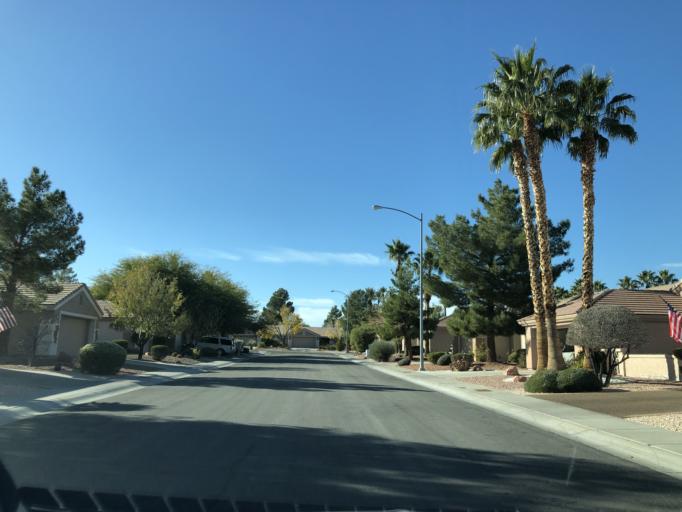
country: US
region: Nevada
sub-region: Clark County
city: Whitney
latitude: 36.0126
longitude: -115.0812
